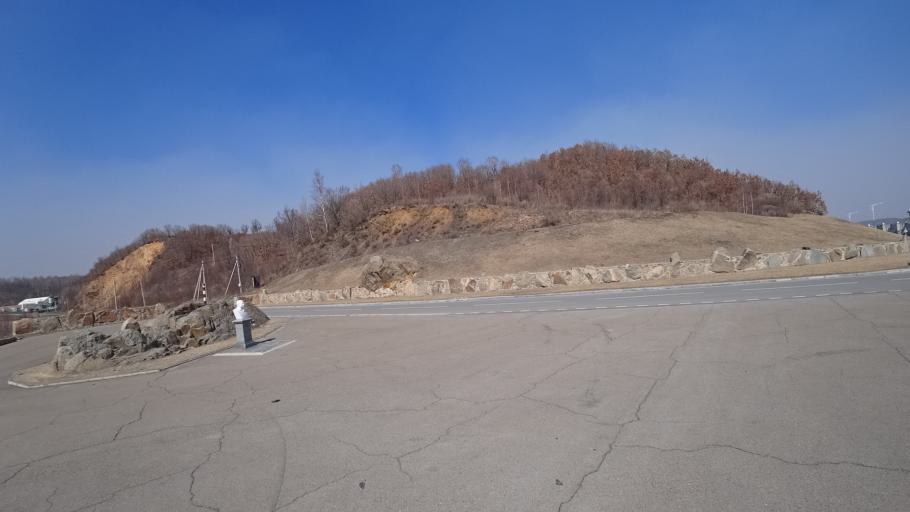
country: RU
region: Amur
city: Novobureyskiy
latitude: 49.7901
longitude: 129.9652
